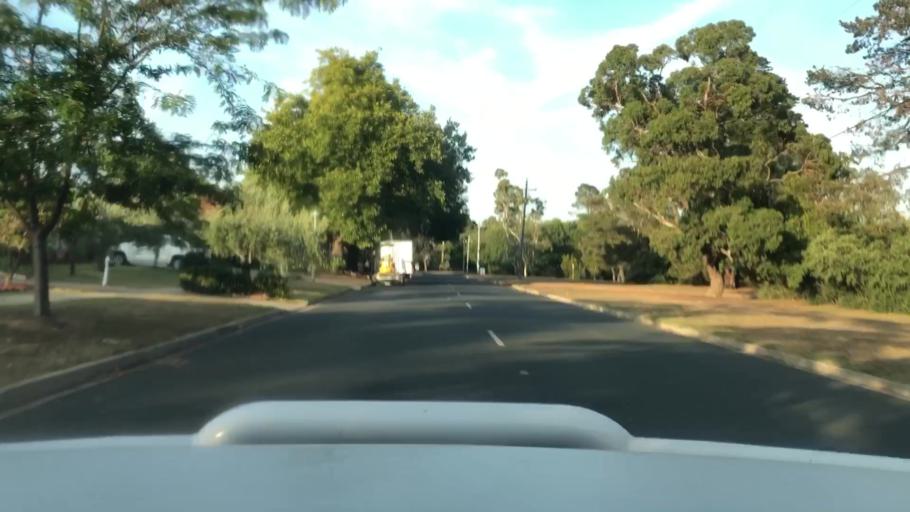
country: AU
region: Australian Capital Territory
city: Canberra
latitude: -35.2525
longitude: 149.1612
